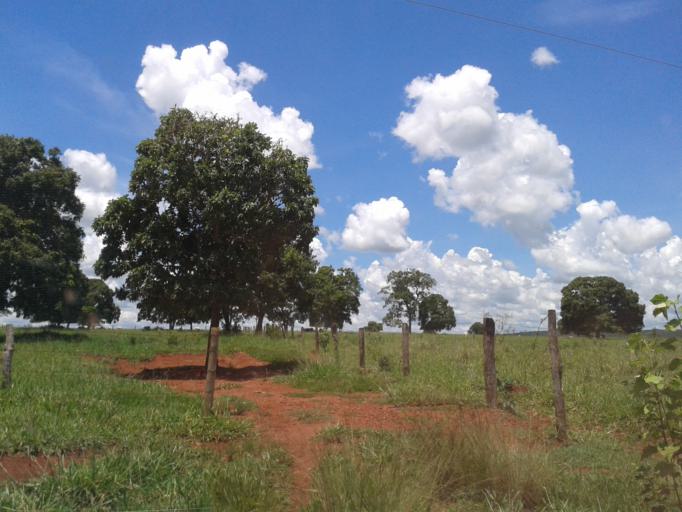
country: BR
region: Minas Gerais
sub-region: Santa Vitoria
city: Santa Vitoria
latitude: -18.7919
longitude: -49.8619
